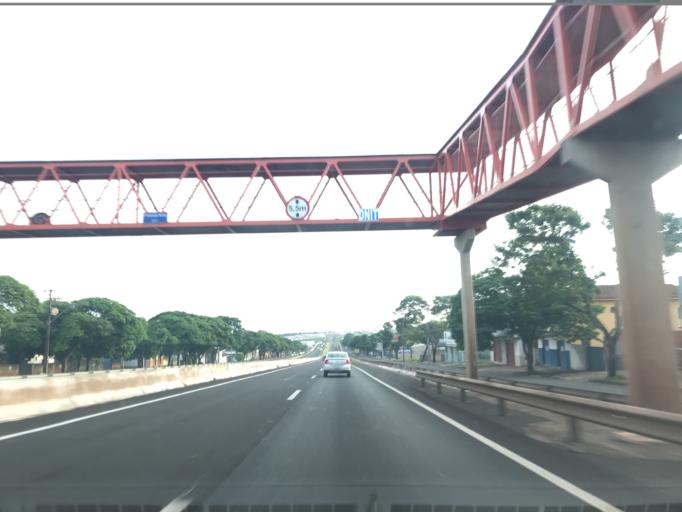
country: BR
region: Parana
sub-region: Maringa
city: Maringa
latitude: -23.4000
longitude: -51.9782
